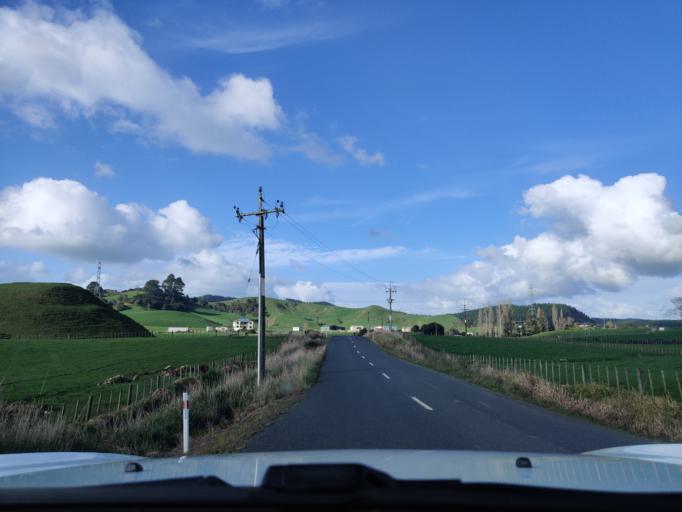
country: NZ
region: Waikato
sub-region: Waikato District
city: Te Kauwhata
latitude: -37.2857
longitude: 175.2127
